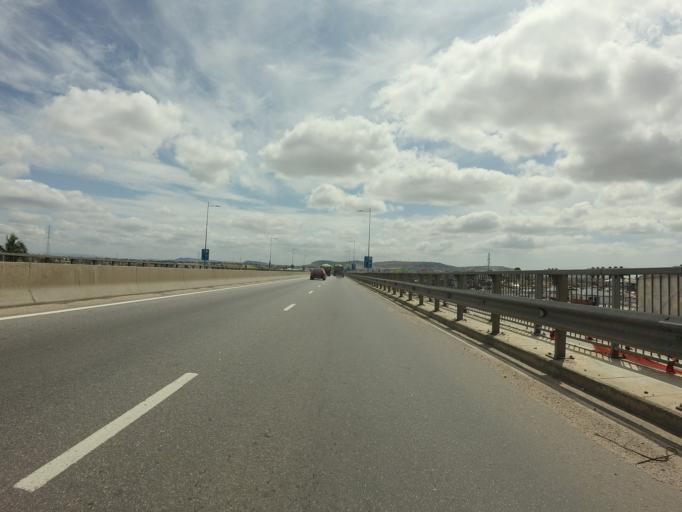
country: GH
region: Central
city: Kasoa
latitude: 5.5342
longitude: -0.4253
